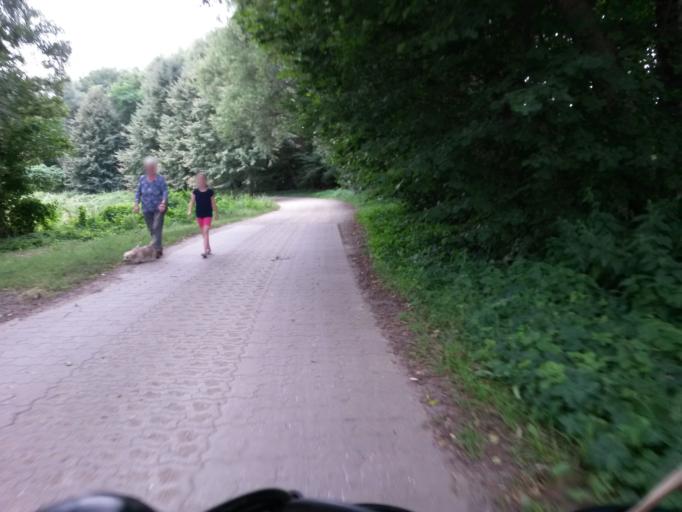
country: DE
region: Brandenburg
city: Angermunde
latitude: 53.0367
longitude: 13.9449
